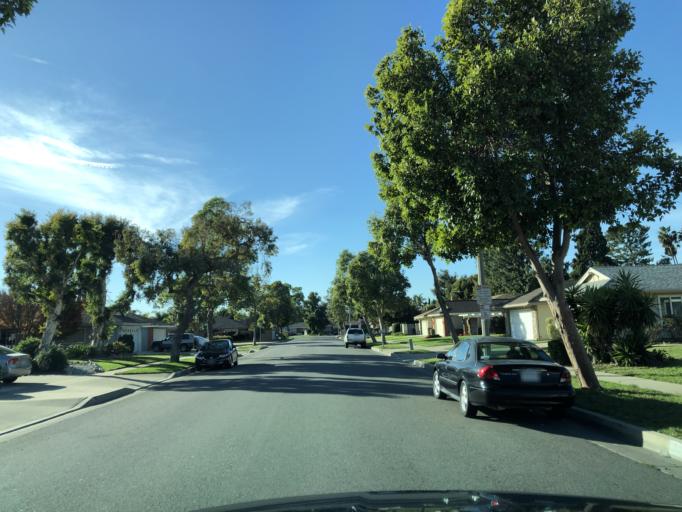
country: US
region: California
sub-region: Orange County
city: Tustin
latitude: 33.7646
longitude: -117.8374
